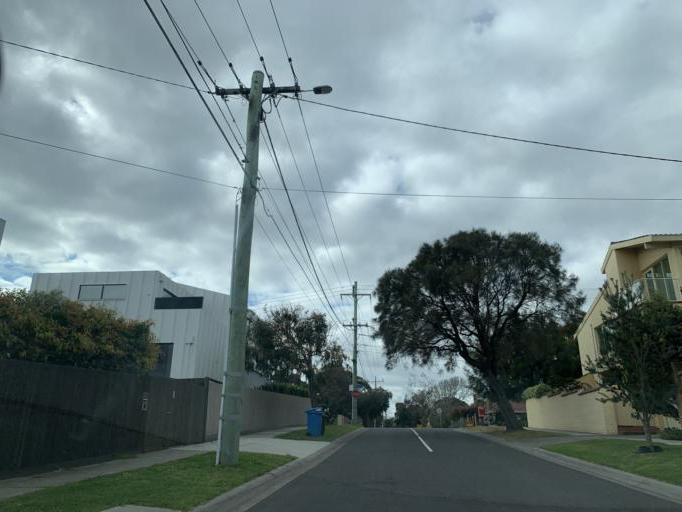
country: AU
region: Victoria
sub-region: Bayside
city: Black Rock
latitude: -37.9811
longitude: 145.0209
